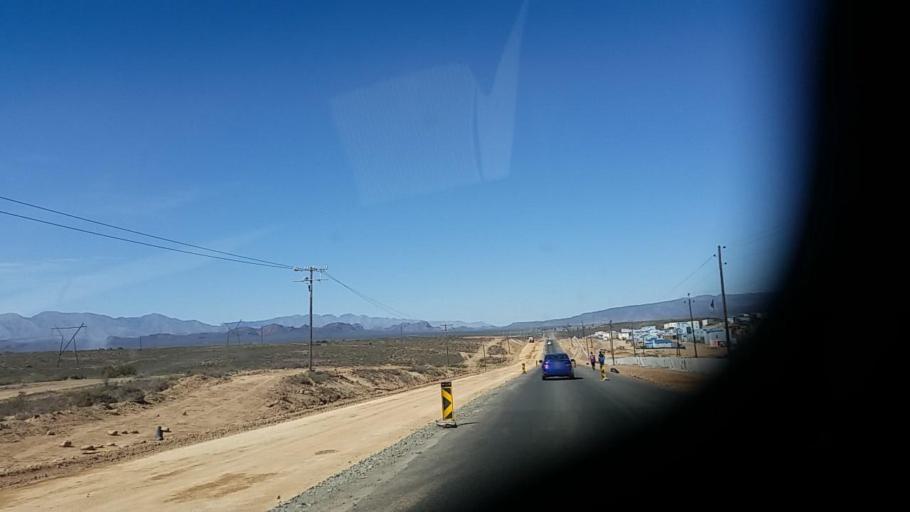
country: ZA
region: Western Cape
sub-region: Eden District Municipality
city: Oudtshoorn
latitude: -33.5899
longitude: 22.2513
